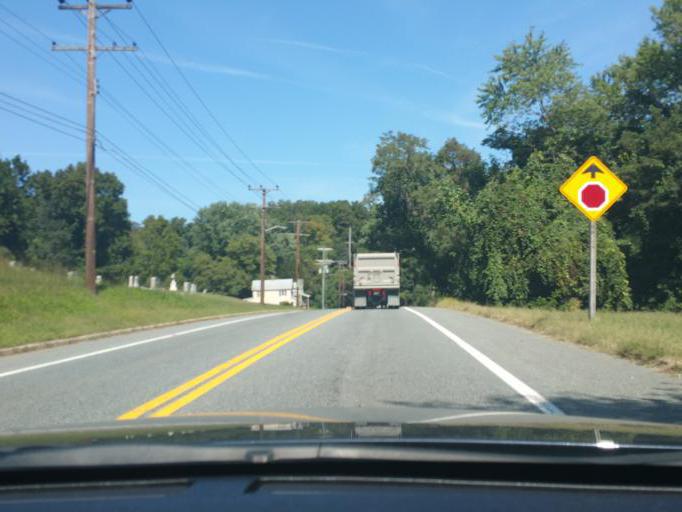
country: US
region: Maryland
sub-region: Harford County
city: Havre de Grace
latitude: 39.5560
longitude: -76.1022
